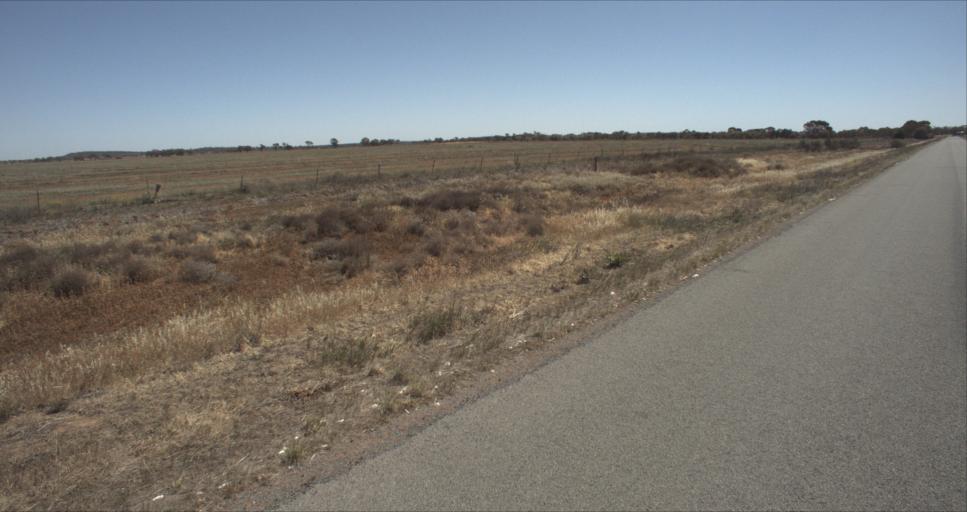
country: AU
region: New South Wales
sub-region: Leeton
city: Leeton
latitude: -34.4355
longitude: 146.2988
